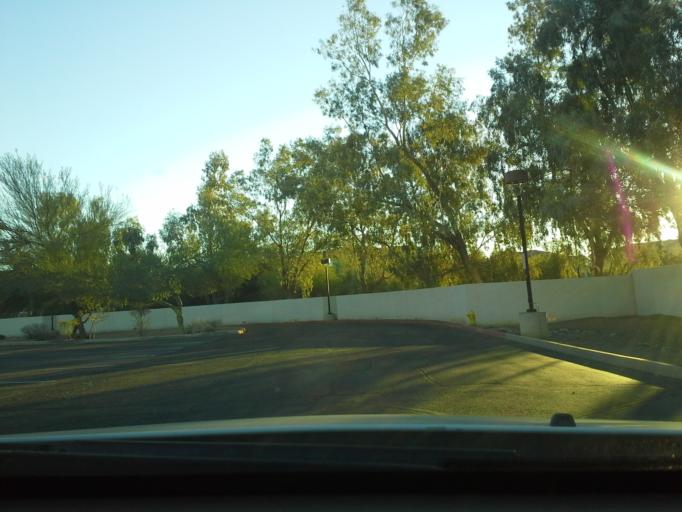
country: US
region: Arizona
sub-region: Maricopa County
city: Guadalupe
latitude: 33.3463
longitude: -111.9584
